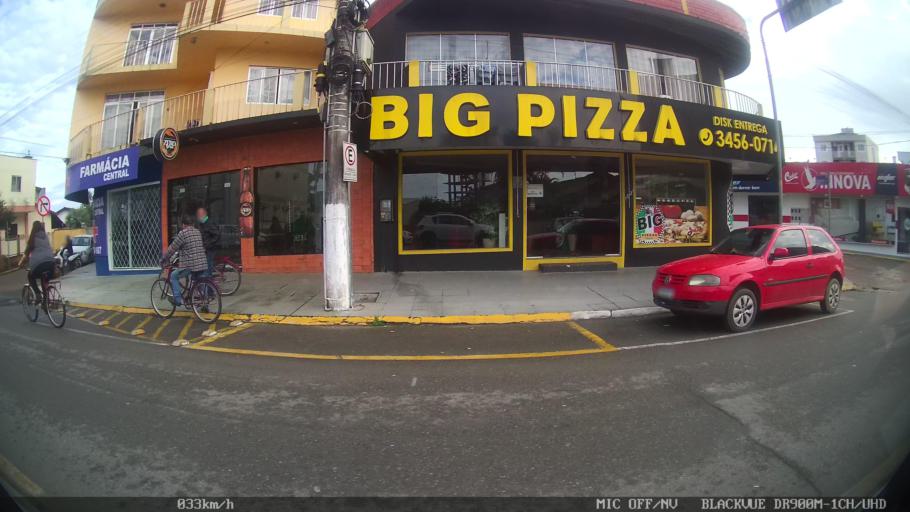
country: BR
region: Santa Catarina
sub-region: Barra Velha
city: Barra Velha
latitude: -26.6447
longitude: -48.6864
